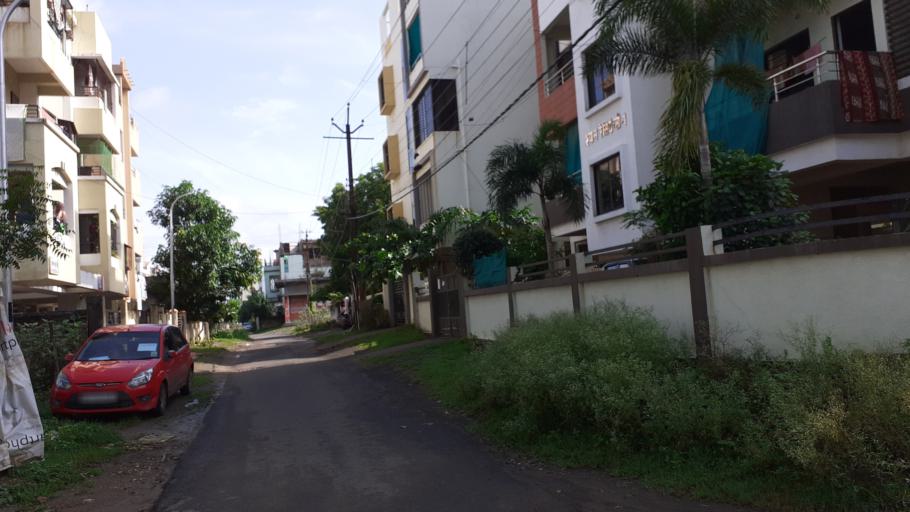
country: IN
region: Maharashtra
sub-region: Nagpur Division
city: Nagpur
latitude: 21.0981
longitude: 79.1091
